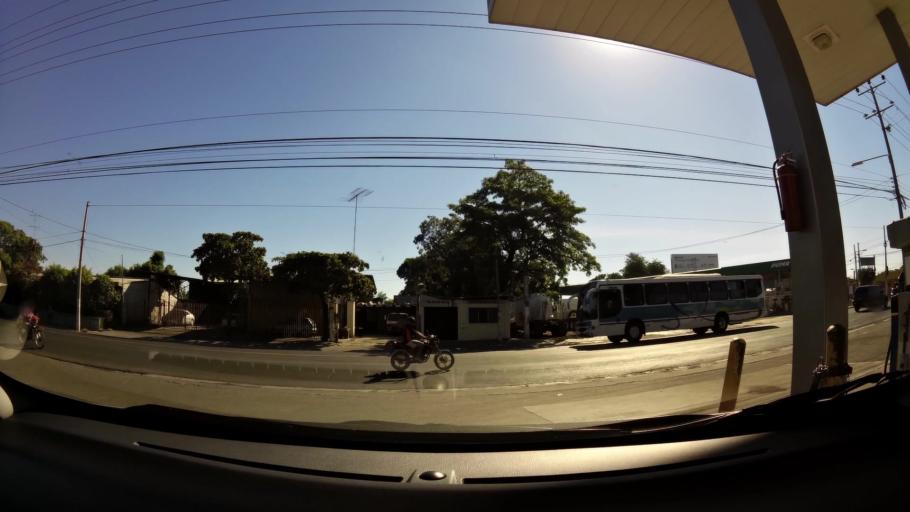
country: SV
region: San Miguel
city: San Miguel
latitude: 13.4677
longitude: -88.1755
